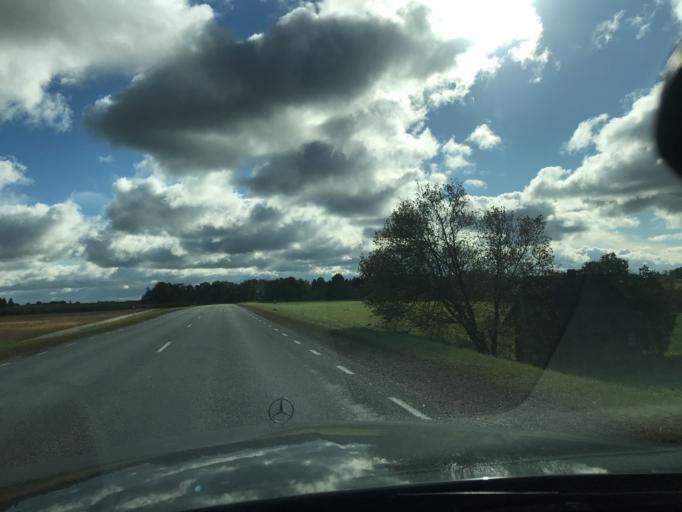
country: EE
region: Vorumaa
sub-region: Antsla vald
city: Vana-Antsla
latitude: 57.9441
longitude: 26.3011
